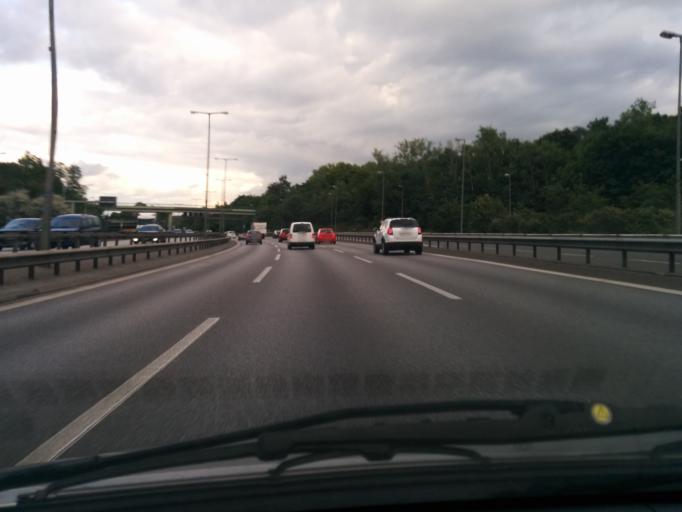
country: DE
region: Berlin
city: Schoneberg Bezirk
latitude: 52.4736
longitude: 13.3530
